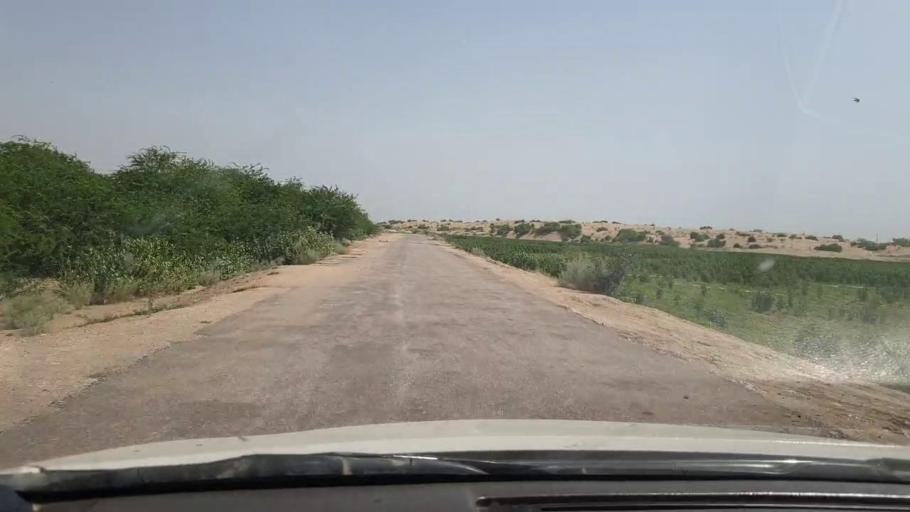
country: PK
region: Sindh
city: Rohri
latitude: 27.4985
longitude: 69.0430
